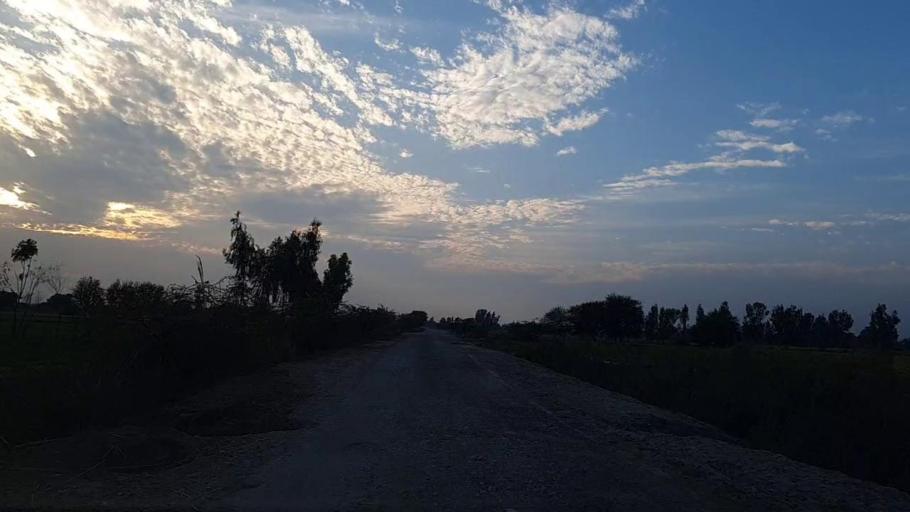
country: PK
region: Sindh
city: Daur
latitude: 26.4170
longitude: 68.4821
